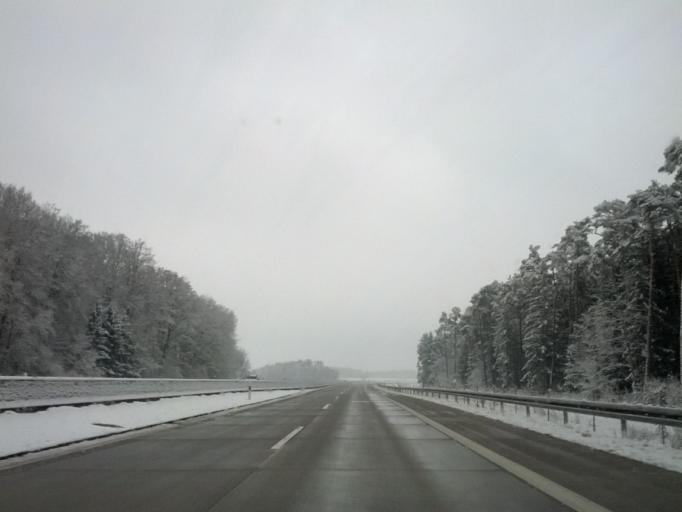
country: DE
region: Bavaria
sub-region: Regierungsbezirk Unterfranken
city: Strahlungen
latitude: 50.2830
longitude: 10.2602
